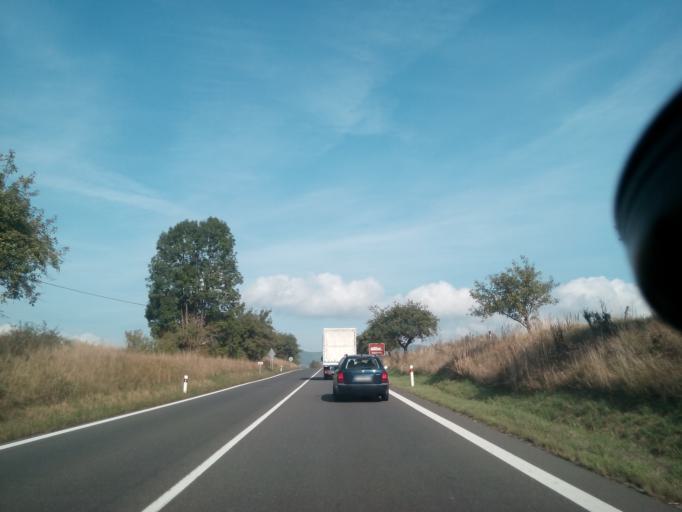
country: SK
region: Kosicky
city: Roznava
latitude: 48.6351
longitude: 20.6148
